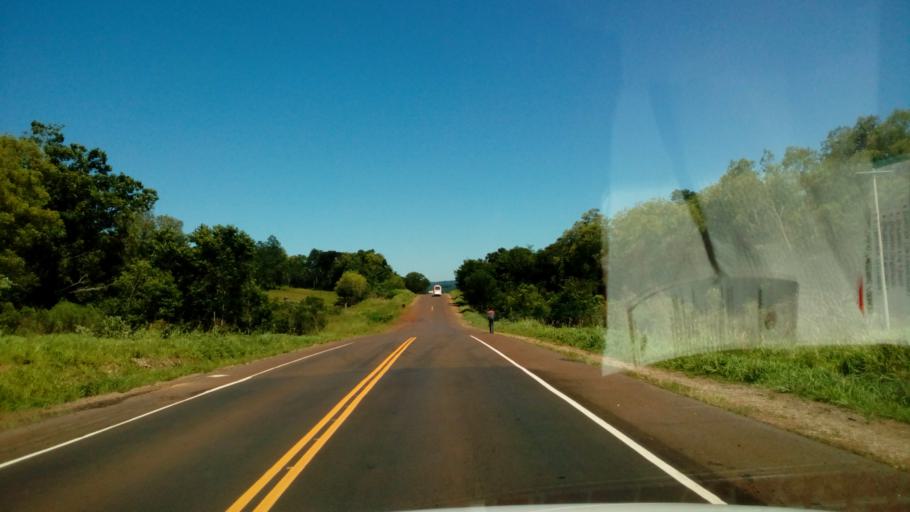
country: AR
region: Misiones
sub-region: Departamento de Leandro N. Alem
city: Leandro N. Alem
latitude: -27.5817
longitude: -55.3707
